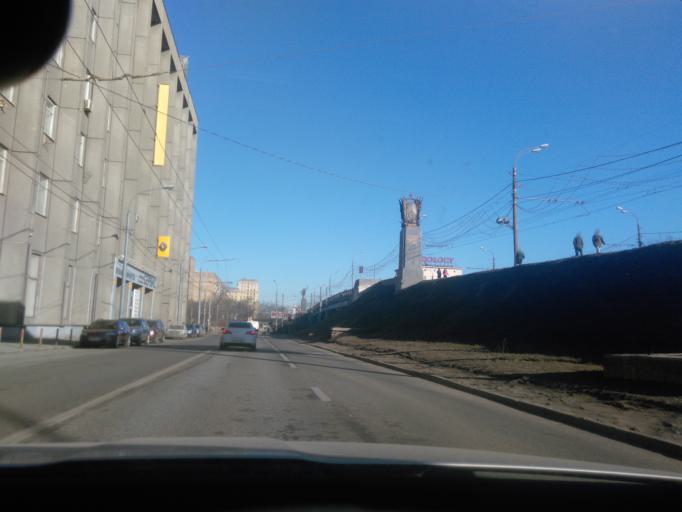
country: RU
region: Moskovskaya
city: Koptevo
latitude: 55.8135
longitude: 37.5017
